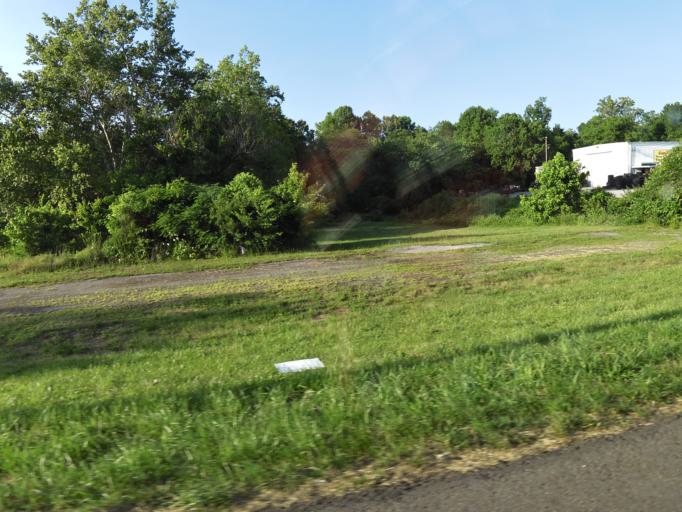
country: US
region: Tennessee
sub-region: Knox County
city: Knoxville
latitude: 35.9069
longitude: -83.8356
